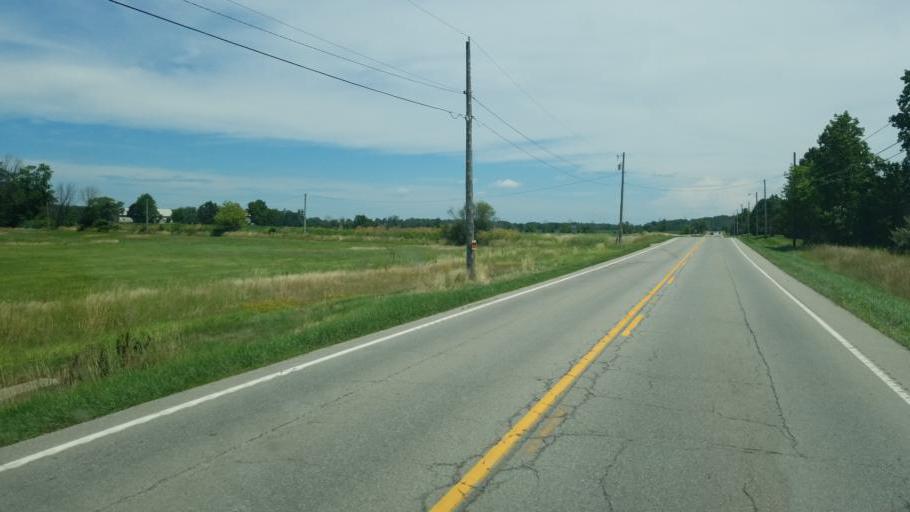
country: US
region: Ohio
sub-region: Richland County
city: Shelby
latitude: 40.8807
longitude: -82.6160
